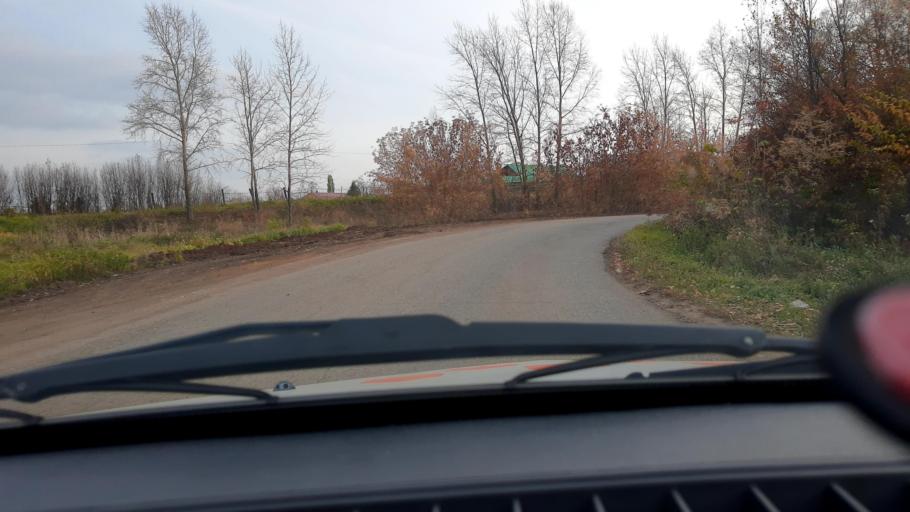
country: RU
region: Bashkortostan
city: Iglino
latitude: 54.7978
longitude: 56.3140
